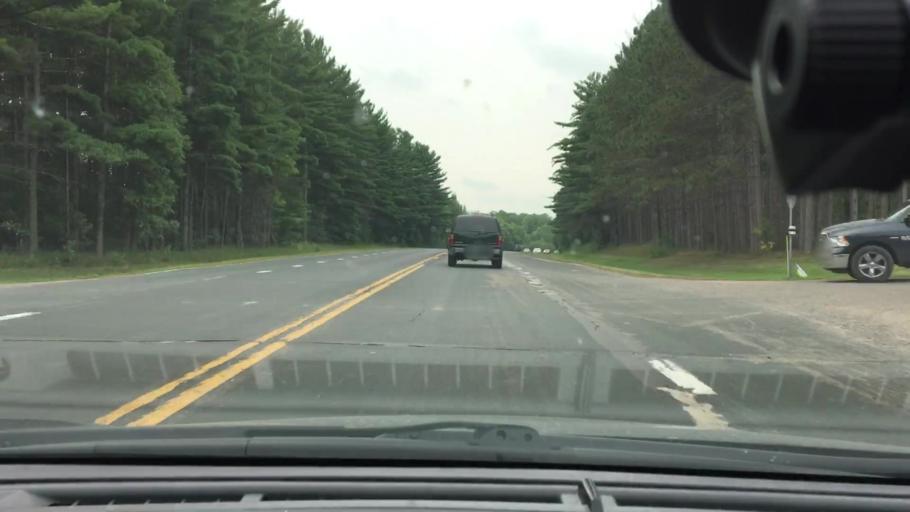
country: US
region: Minnesota
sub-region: Mille Lacs County
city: Vineland
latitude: 46.2252
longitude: -93.7923
